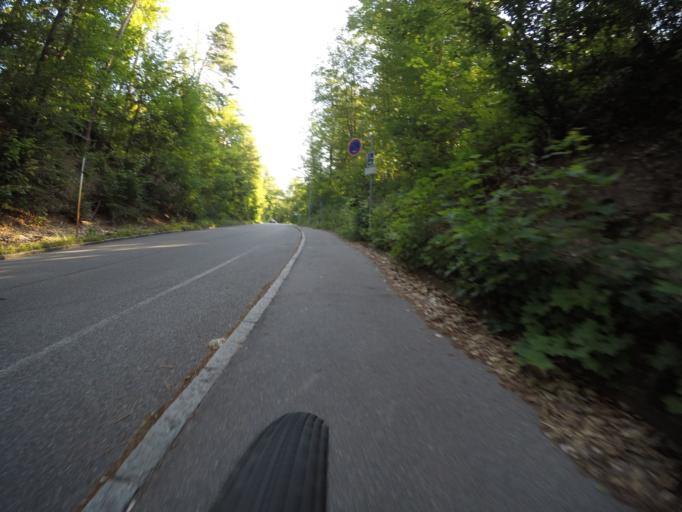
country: DE
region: Baden-Wuerttemberg
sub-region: Regierungsbezirk Stuttgart
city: Sindelfingen
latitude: 48.7162
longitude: 9.0238
